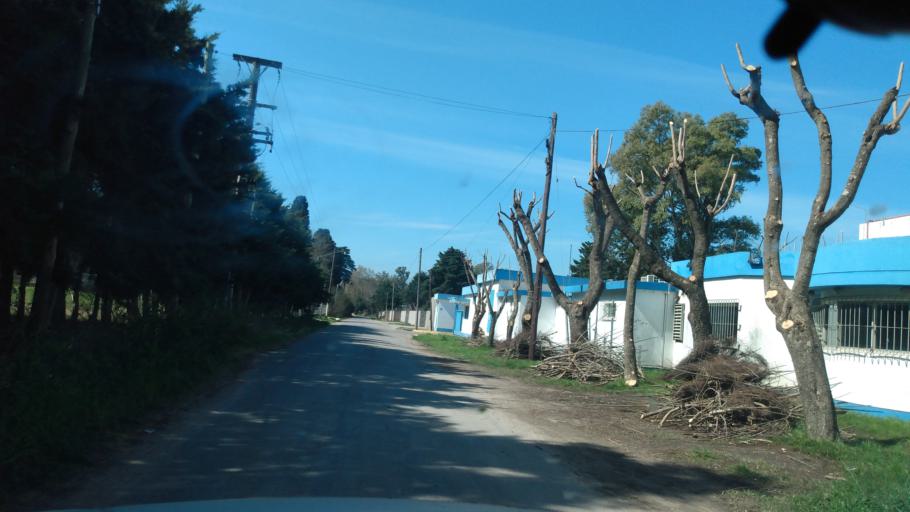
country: AR
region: Buenos Aires
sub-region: Partido de Lujan
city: Lujan
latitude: -34.5736
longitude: -59.1326
